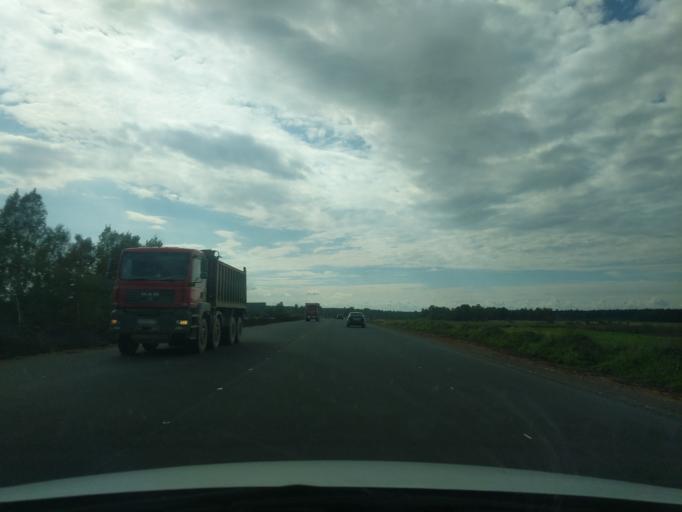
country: RU
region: Kostroma
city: Sudislavl'
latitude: 57.8313
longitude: 41.5443
